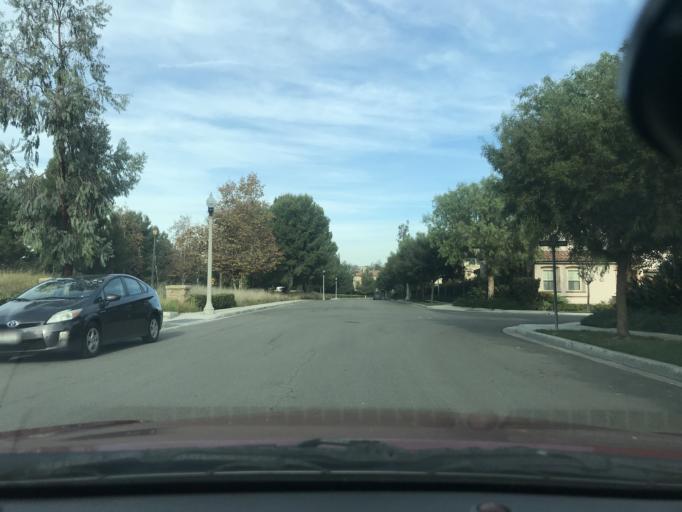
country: US
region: California
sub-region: Orange County
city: Irvine
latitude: 33.6998
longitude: -117.7574
